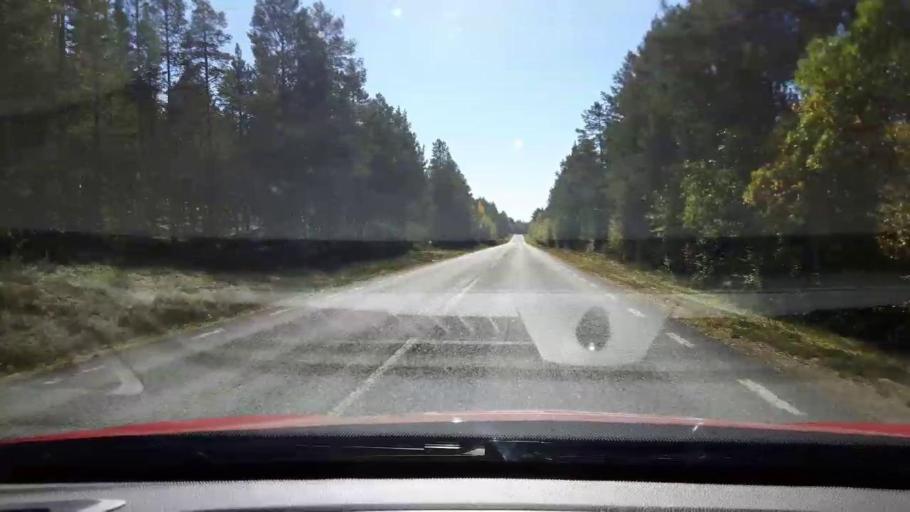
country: SE
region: Jaemtland
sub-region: Harjedalens Kommun
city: Sveg
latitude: 62.3317
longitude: 14.0564
